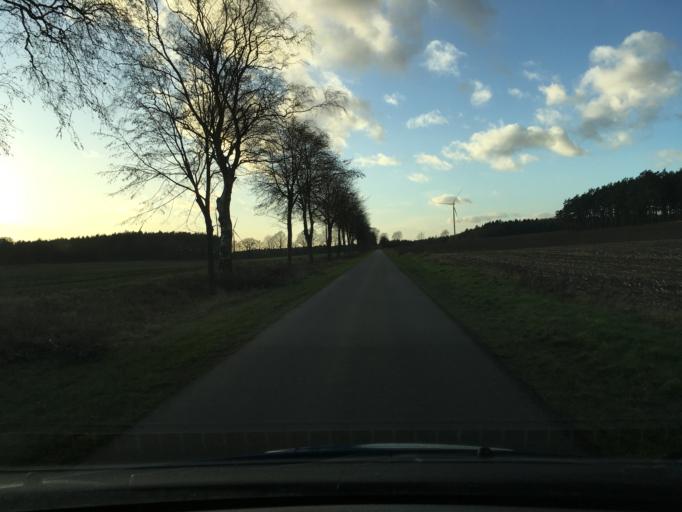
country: DE
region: Lower Saxony
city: Rehlingen
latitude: 53.1032
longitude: 10.2023
